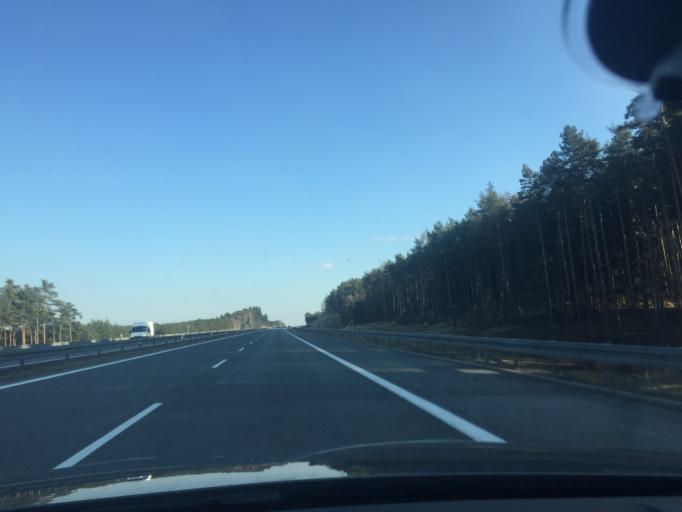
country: PL
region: Lubusz
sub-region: Powiat miedzyrzecki
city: Brojce
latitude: 52.3131
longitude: 15.6051
